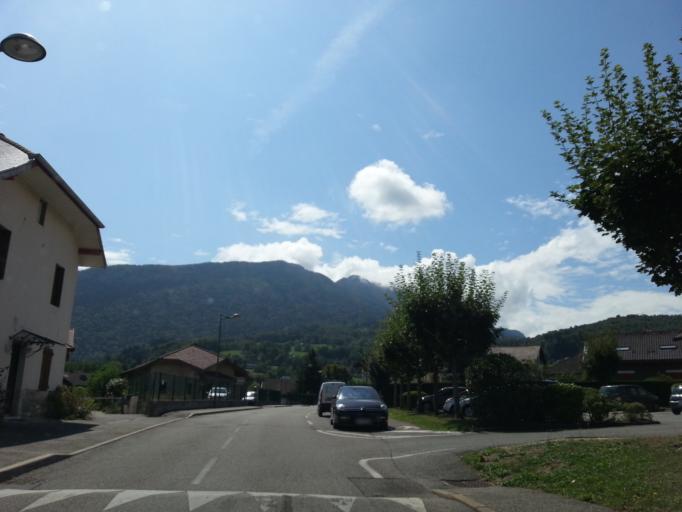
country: FR
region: Rhone-Alpes
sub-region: Departement de la Haute-Savoie
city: Saint-Jorioz
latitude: 45.8310
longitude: 6.1656
